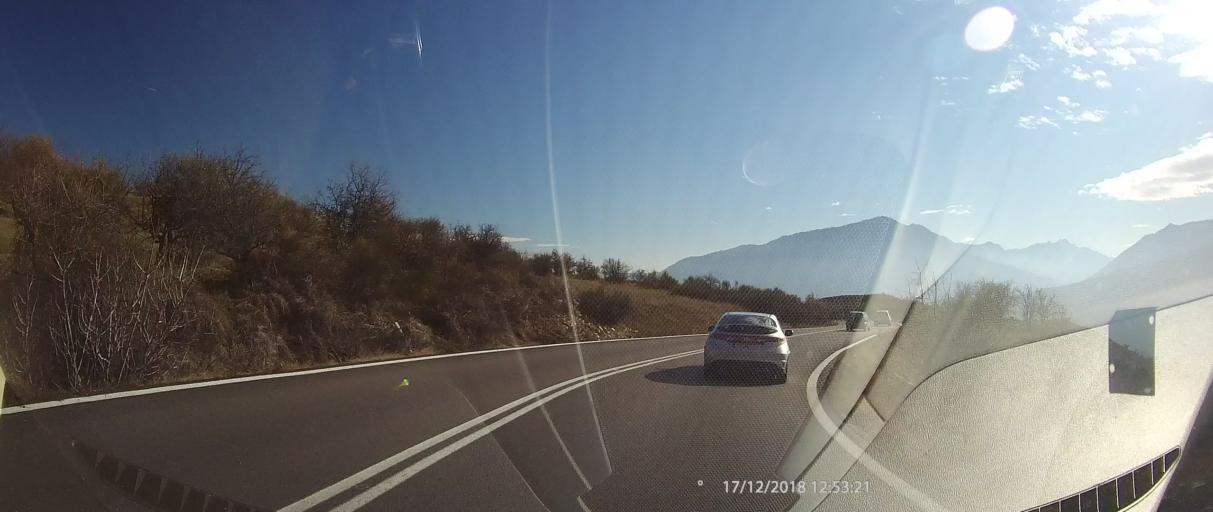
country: GR
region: Thessaly
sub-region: Trikala
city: Kastraki
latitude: 39.7561
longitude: 21.4902
